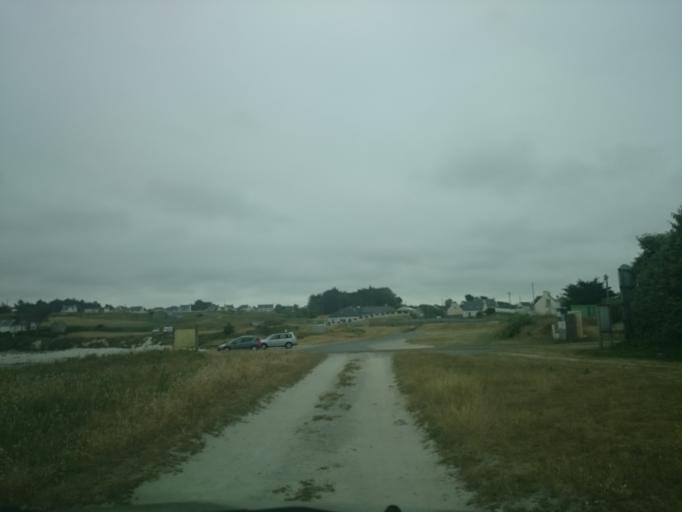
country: FR
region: Brittany
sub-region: Departement du Finistere
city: Saint-Pabu
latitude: 48.5767
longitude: -4.6268
